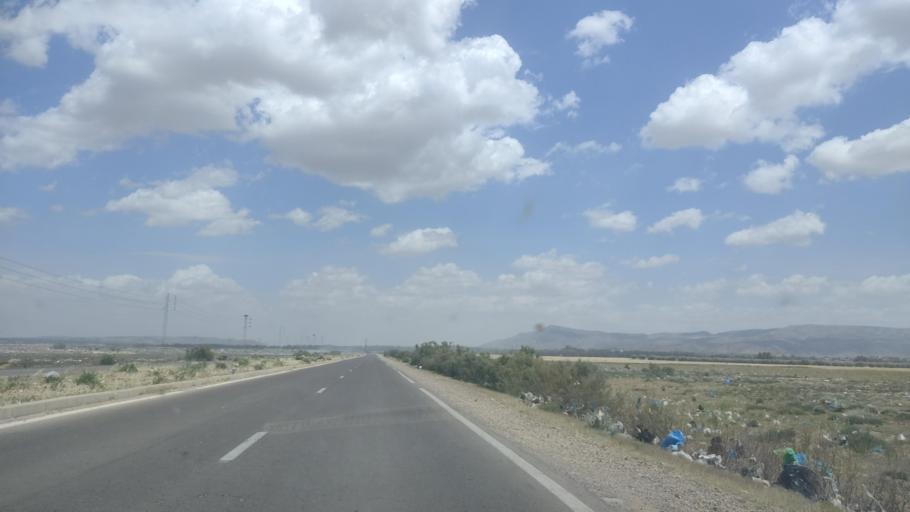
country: TN
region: Al Qasrayn
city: Kasserine
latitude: 35.1993
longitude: 8.8444
